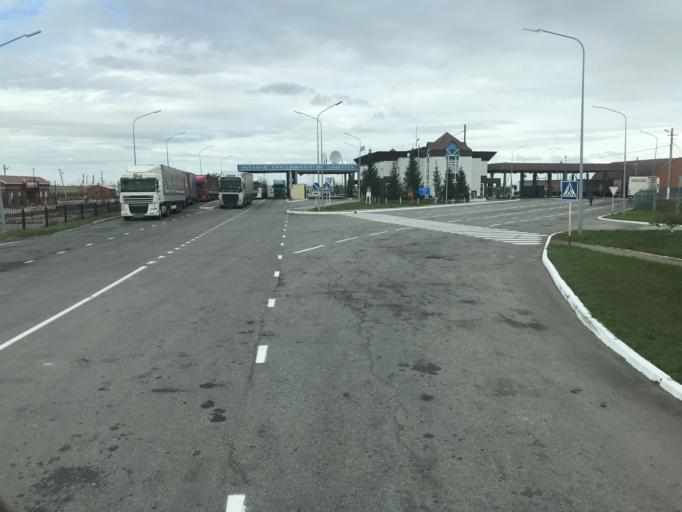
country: RU
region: Chelyabinsk
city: Bobrovka
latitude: 53.9997
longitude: 61.6398
